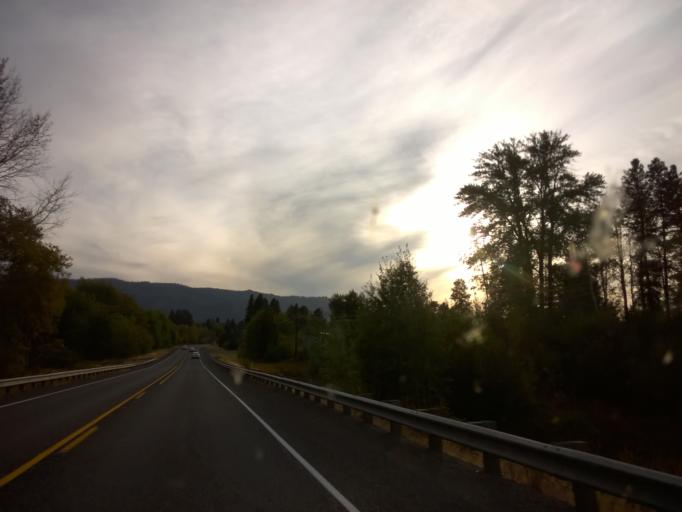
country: US
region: Washington
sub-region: Kittitas County
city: Cle Elum
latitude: 47.1773
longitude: -120.8443
